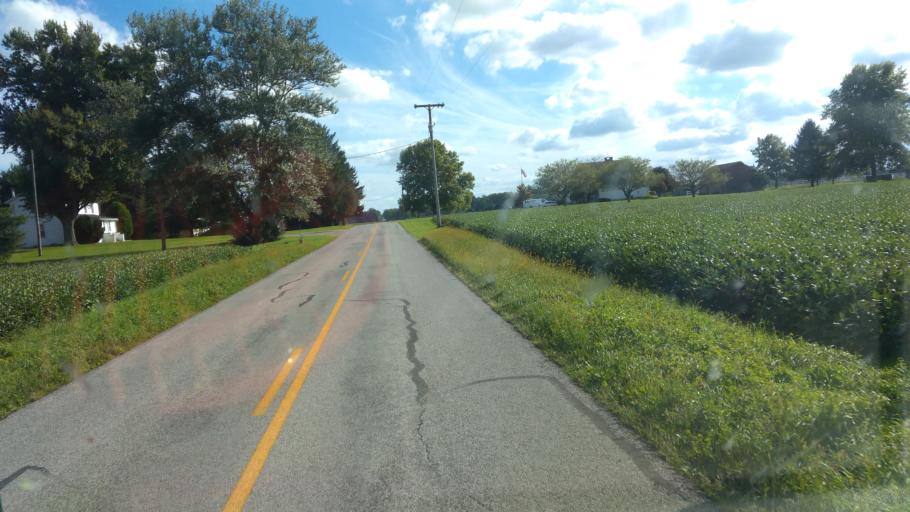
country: US
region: Ohio
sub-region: Sandusky County
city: Mount Carmel
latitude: 41.2792
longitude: -82.9558
